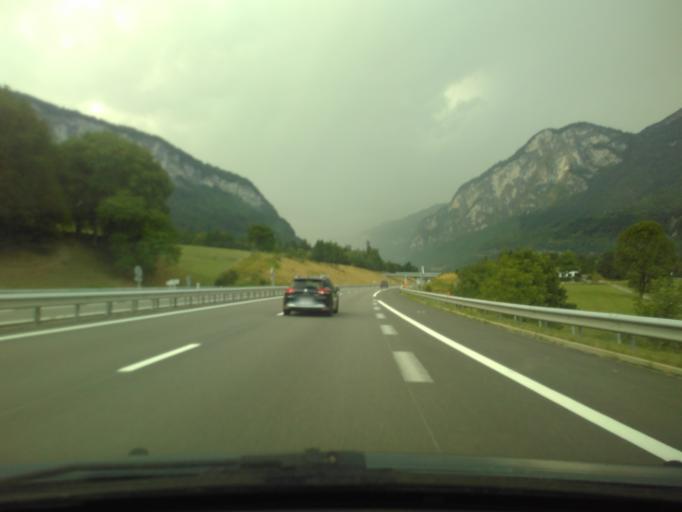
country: FR
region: Rhone-Alpes
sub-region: Departement de la Haute-Savoie
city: Sallanches
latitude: 45.9684
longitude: 6.6274
